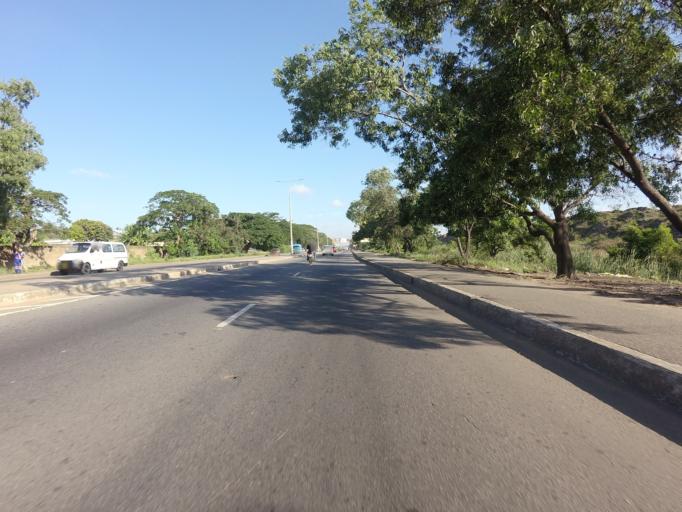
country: GH
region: Greater Accra
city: Accra
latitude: 5.5450
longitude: -0.2272
